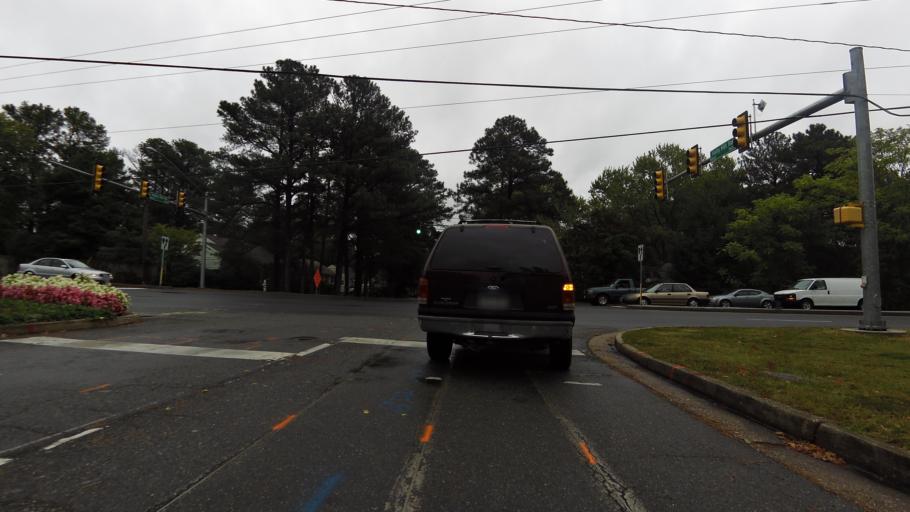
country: US
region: Virginia
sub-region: Henrico County
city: Tuckahoe
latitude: 37.5996
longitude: -77.5643
